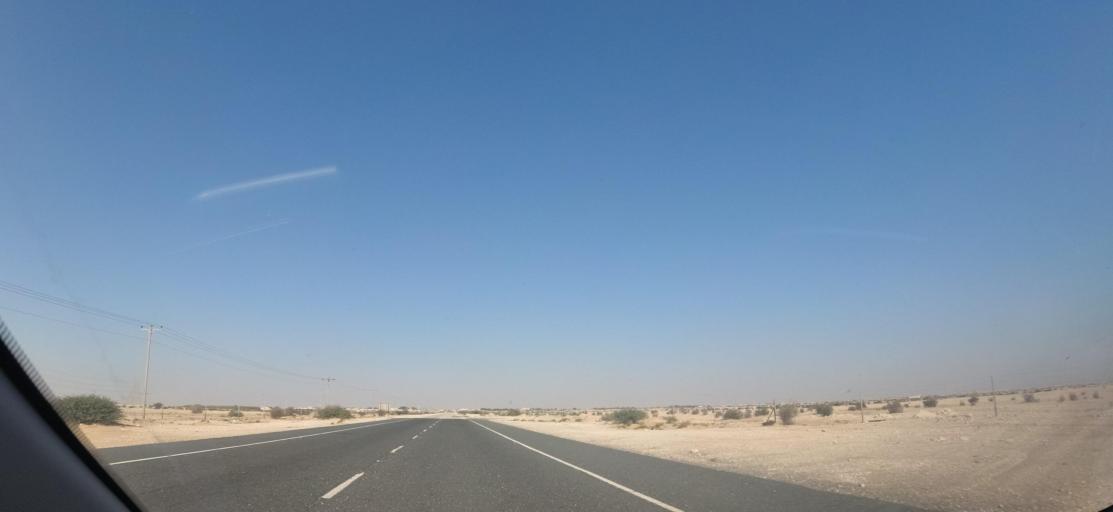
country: QA
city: Al Jumayliyah
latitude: 25.5986
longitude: 51.0703
